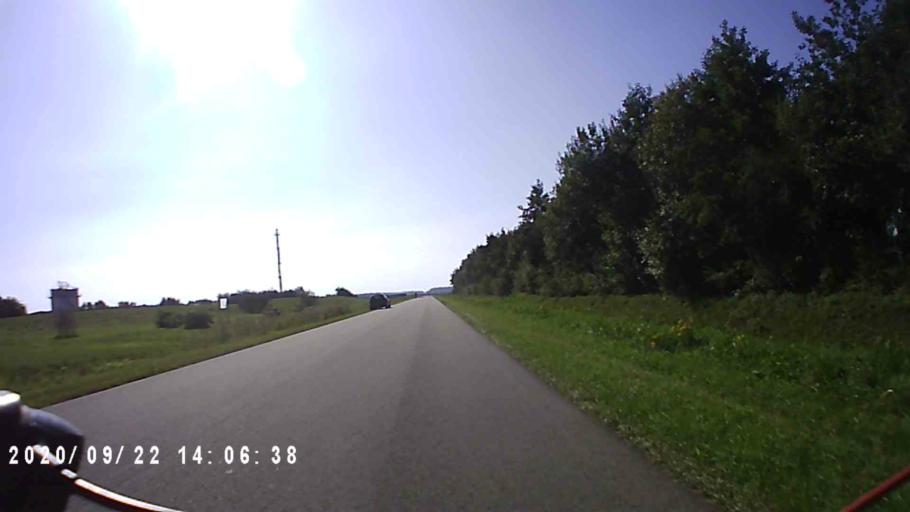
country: NL
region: Groningen
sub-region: Gemeente Leek
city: Leek
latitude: 53.0928
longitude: 6.4267
